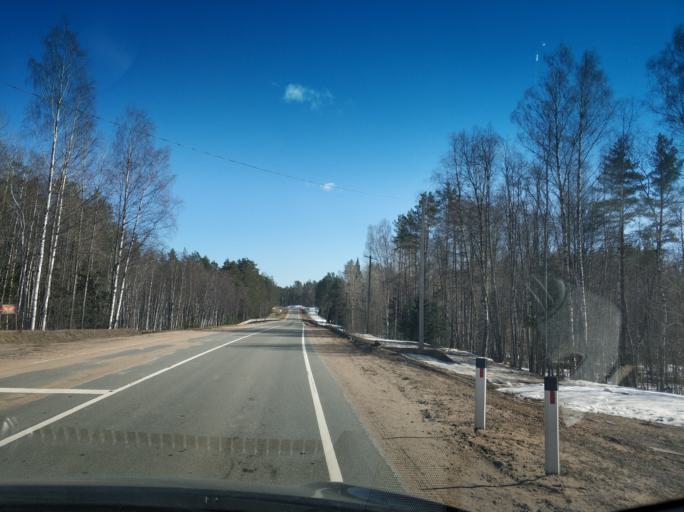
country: RU
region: Leningrad
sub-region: Vsevolzhskij Rajon
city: Vaskelovo
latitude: 60.4256
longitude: 30.2507
